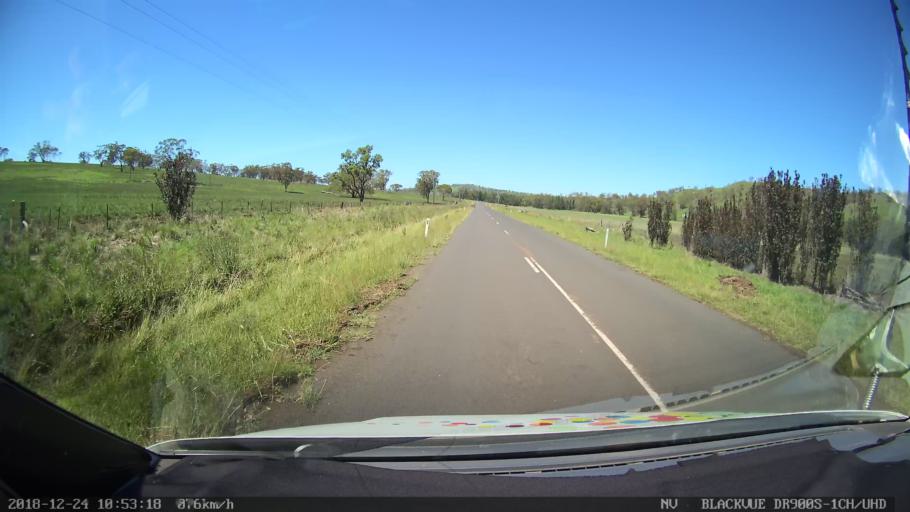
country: AU
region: New South Wales
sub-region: Upper Hunter Shire
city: Merriwa
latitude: -31.9901
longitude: 150.4219
